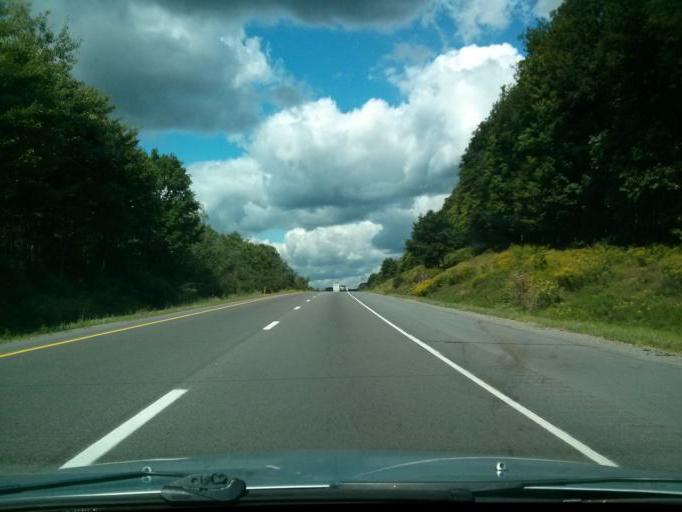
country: US
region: Pennsylvania
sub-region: Clearfield County
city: Treasure Lake
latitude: 41.1336
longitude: -78.7218
